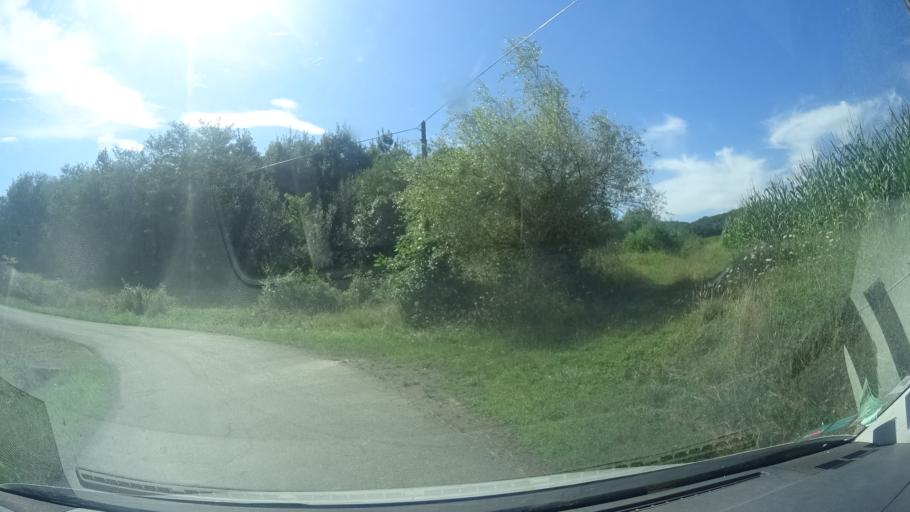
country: FR
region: Aquitaine
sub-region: Departement des Pyrenees-Atlantiques
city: Orthez
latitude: 43.4972
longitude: -0.7054
